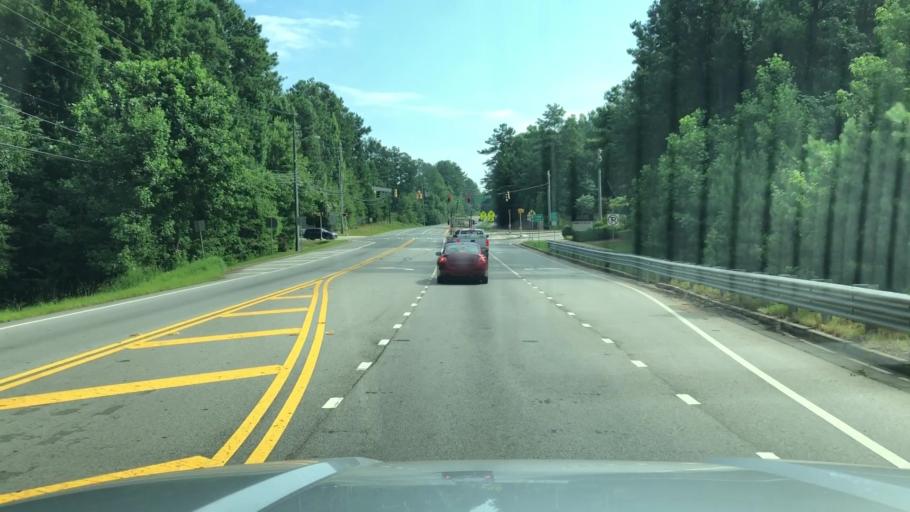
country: US
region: Georgia
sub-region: Cobb County
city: Acworth
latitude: 34.0342
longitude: -84.7392
